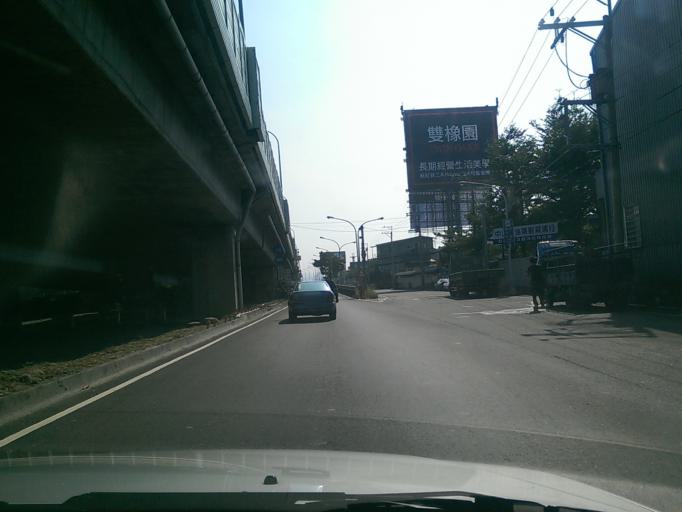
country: TW
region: Taiwan
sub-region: Taichung City
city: Taichung
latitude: 24.1353
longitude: 120.6217
